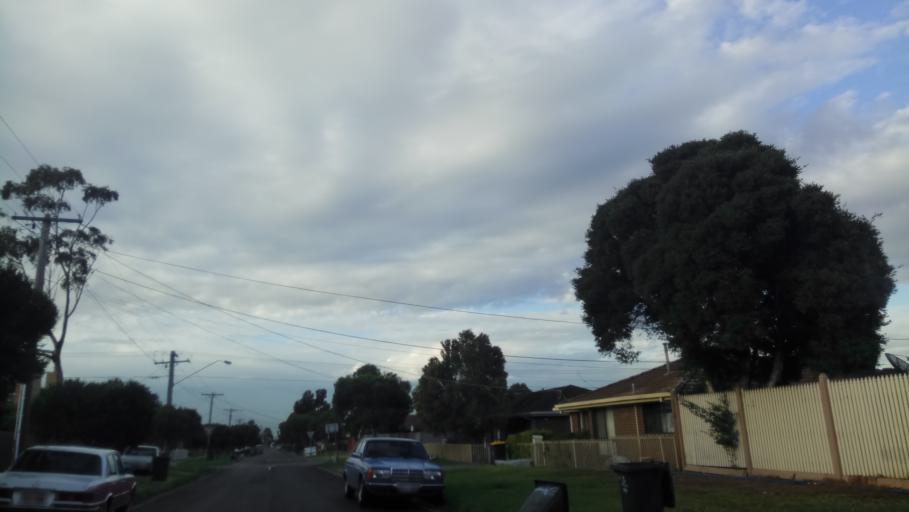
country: AU
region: Victoria
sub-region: Hobsons Bay
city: Laverton
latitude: -37.8679
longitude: 144.7758
